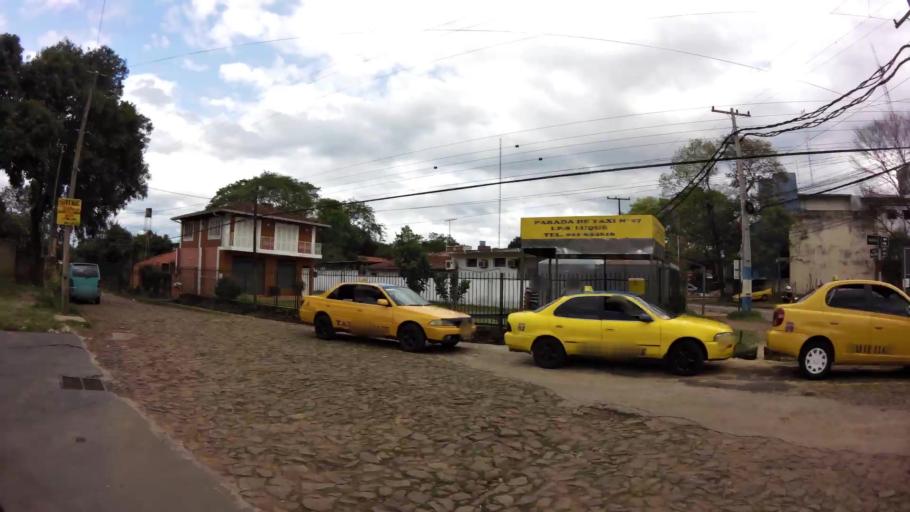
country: PY
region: Central
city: San Lorenzo
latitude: -25.2819
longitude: -57.4837
